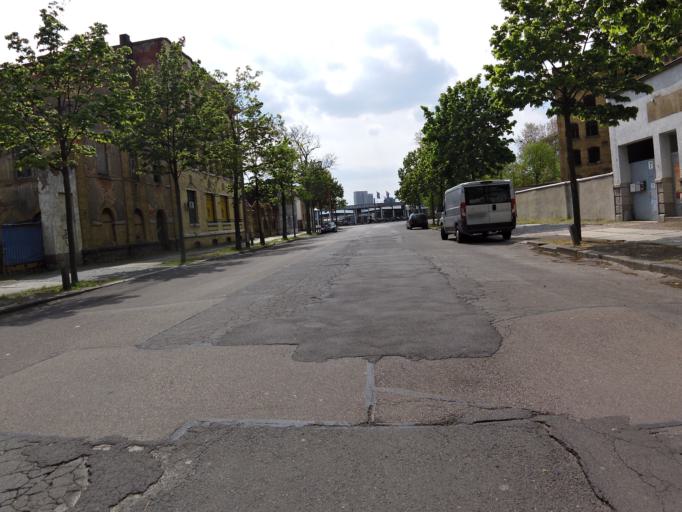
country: DE
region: Saxony
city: Leipzig
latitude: 51.3580
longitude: 12.3885
